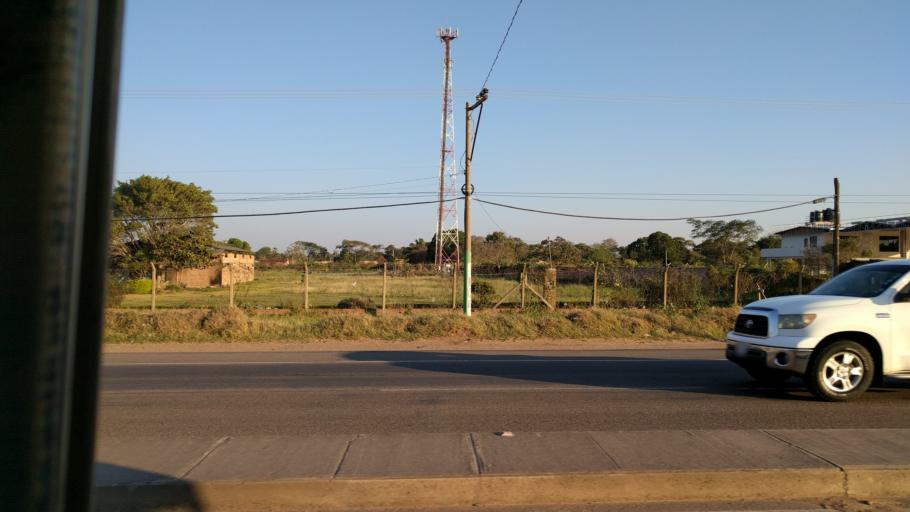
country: BO
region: Santa Cruz
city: Cotoca
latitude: -17.7607
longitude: -63.0198
